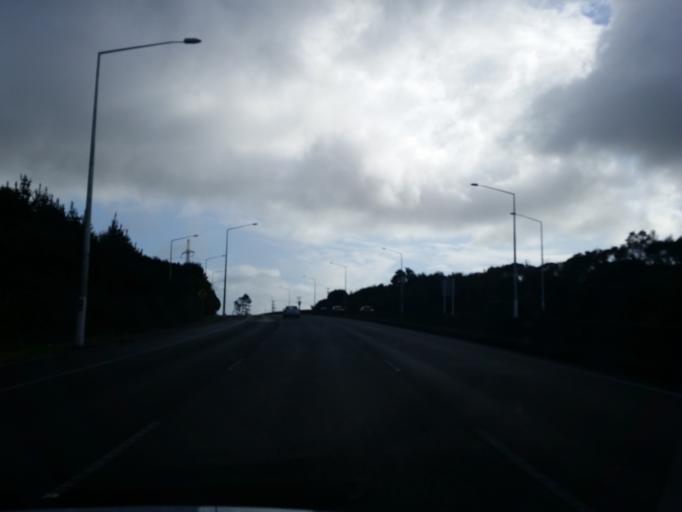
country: NZ
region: Auckland
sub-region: Auckland
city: Pukekohe East
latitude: -37.2145
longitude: 174.9997
